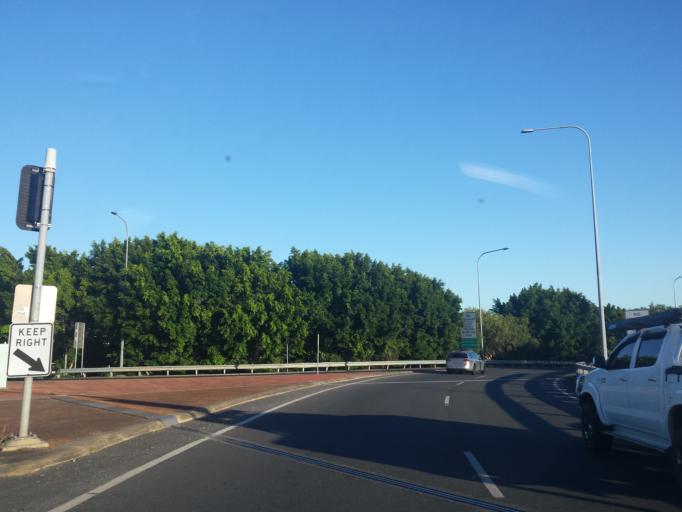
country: AU
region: Queensland
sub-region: Gold Coast
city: Oxenford
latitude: -27.8853
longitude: 153.3155
